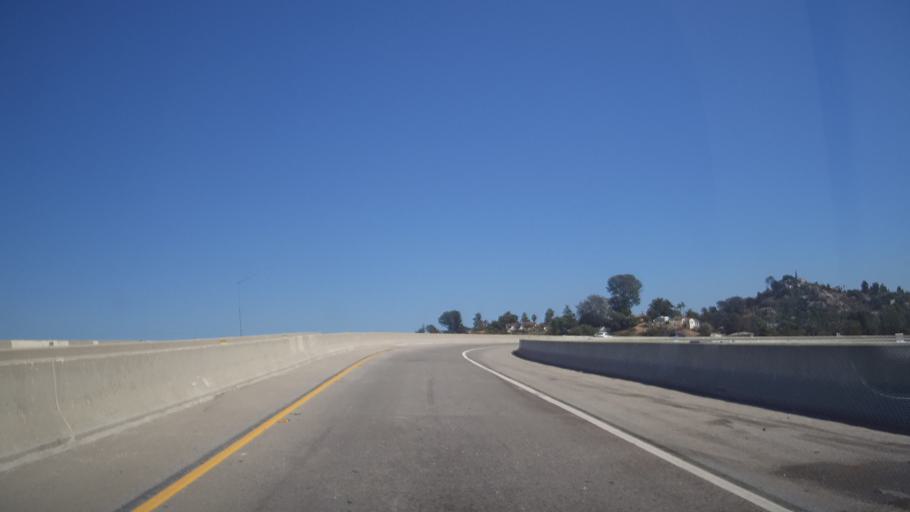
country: US
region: California
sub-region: San Diego County
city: La Mesa
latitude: 32.7759
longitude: -117.0063
